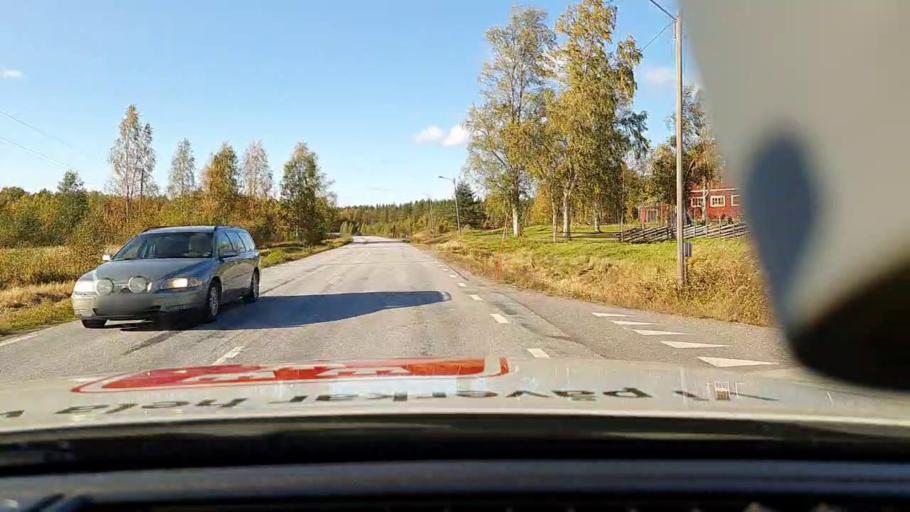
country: SE
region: Norrbotten
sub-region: Pitea Kommun
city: Norrfjarden
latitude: 65.4314
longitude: 21.4891
